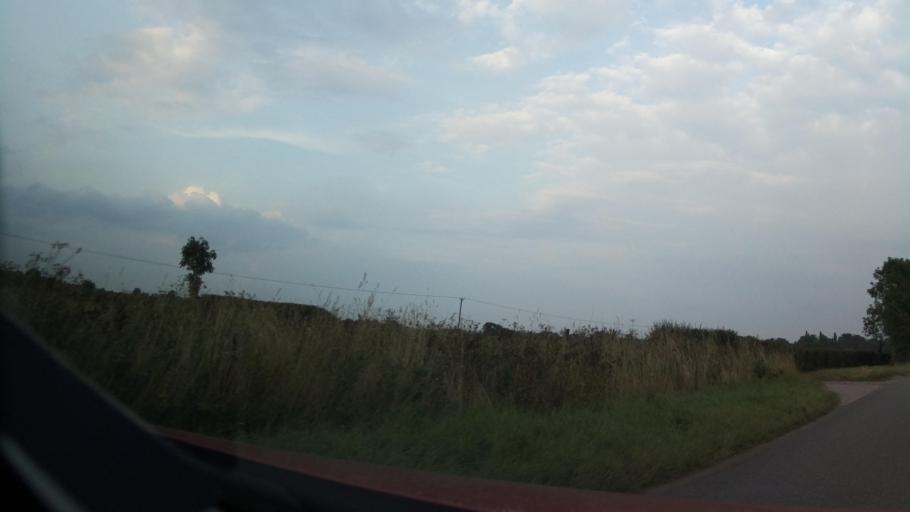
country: GB
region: England
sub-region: Lincolnshire
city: Skellingthorpe
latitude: 53.1430
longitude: -0.6575
